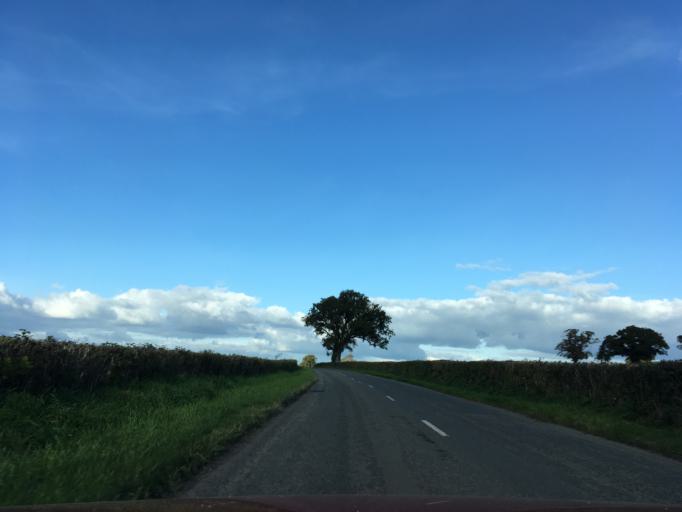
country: GB
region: England
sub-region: Herefordshire
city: Clifford
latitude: 52.0894
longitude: -3.1157
